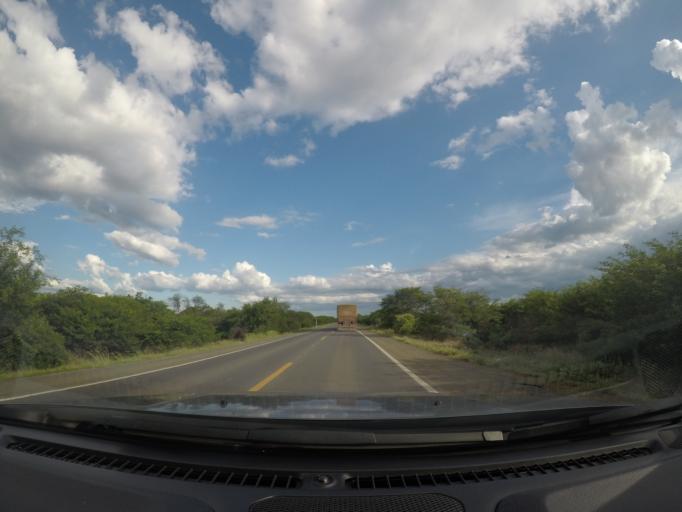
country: BR
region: Bahia
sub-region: Oliveira Dos Brejinhos
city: Beira Rio
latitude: -12.1799
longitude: -42.8351
